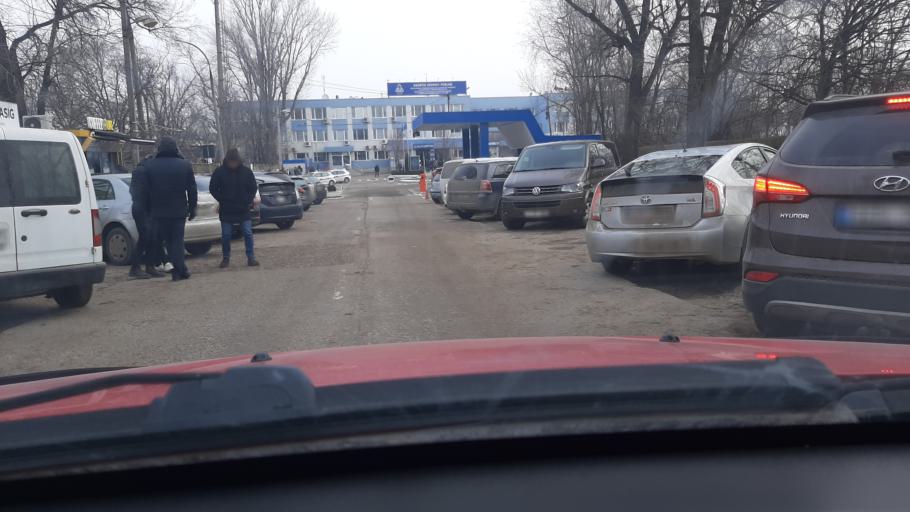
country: MD
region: Chisinau
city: Chisinau
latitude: 46.9750
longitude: 28.8972
